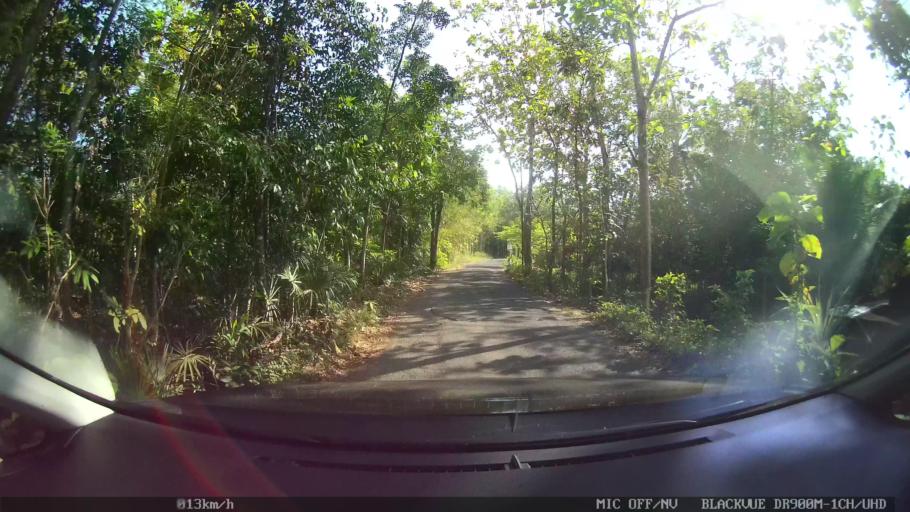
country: ID
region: Daerah Istimewa Yogyakarta
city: Kasihan
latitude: -7.8357
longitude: 110.2858
